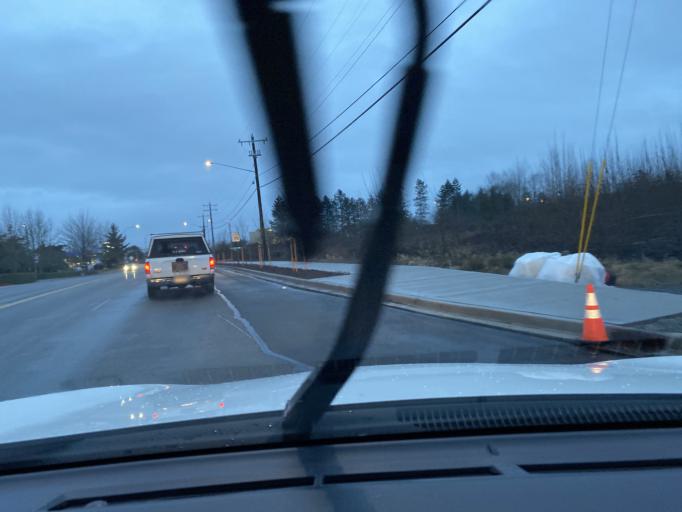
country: US
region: Washington
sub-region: Snohomish County
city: Meadowdale
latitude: 47.8889
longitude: -122.2880
